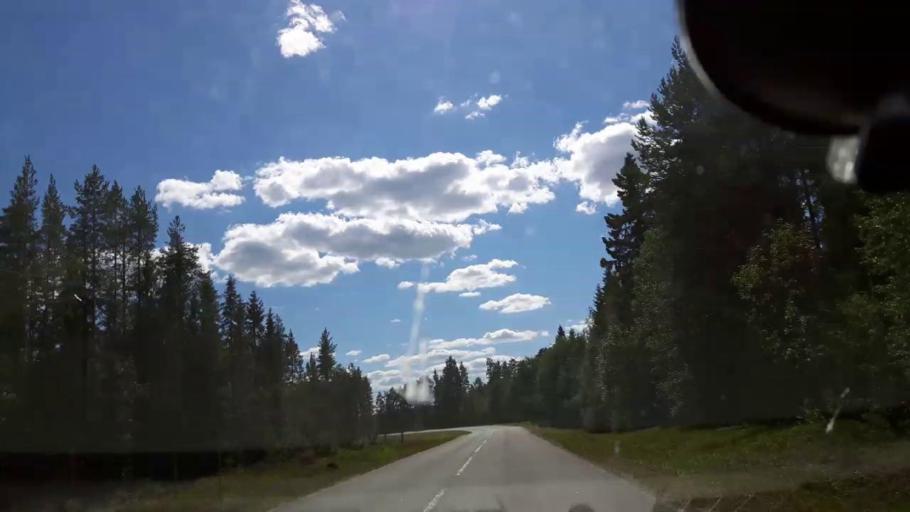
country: SE
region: Jaemtland
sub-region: Ragunda Kommun
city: Hammarstrand
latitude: 62.8804
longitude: 16.2218
